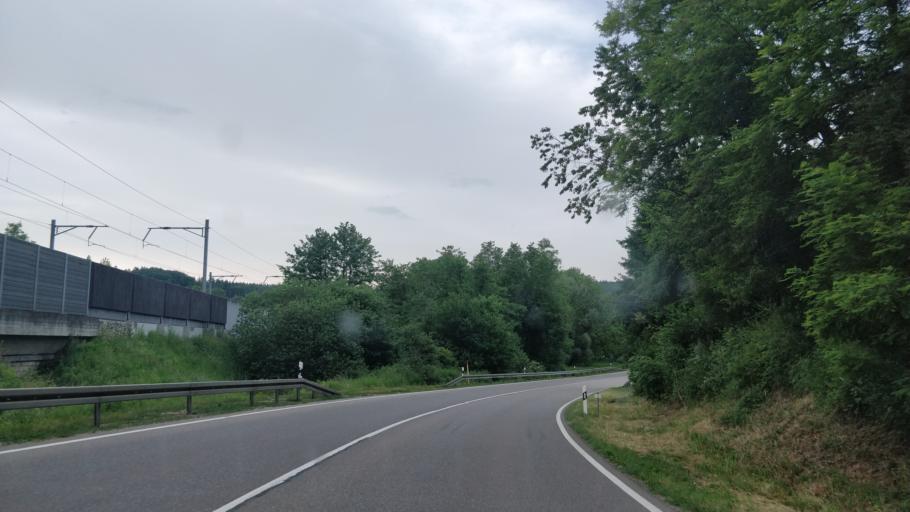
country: DE
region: Baden-Wuerttemberg
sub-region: Freiburg Region
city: Jestetten
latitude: 47.6443
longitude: 8.5639
